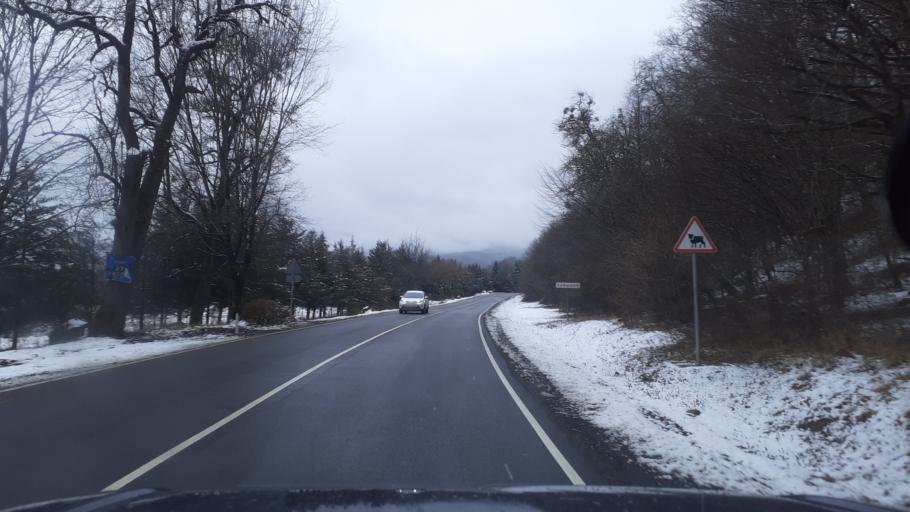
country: RU
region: Adygeya
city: Kamennomostskiy
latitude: 44.1169
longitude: 40.1210
